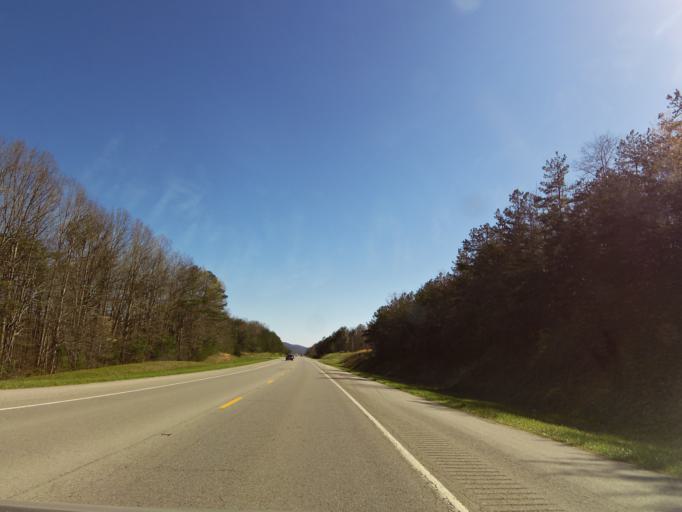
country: US
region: Kentucky
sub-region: McCreary County
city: Pine Knot
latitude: 36.6122
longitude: -84.4396
